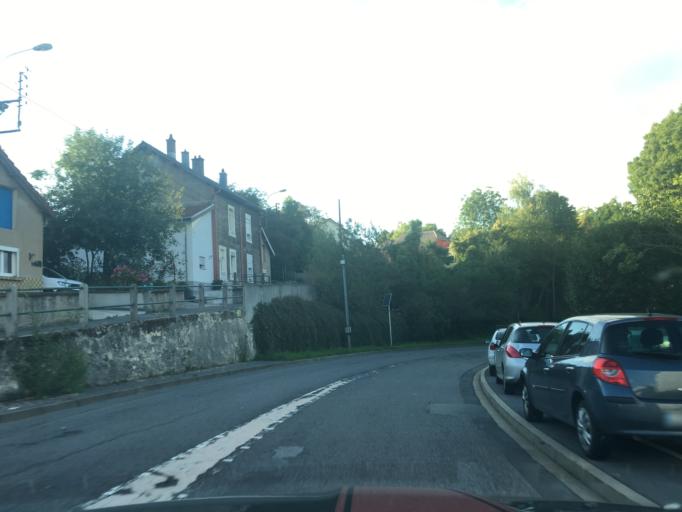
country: FR
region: Lorraine
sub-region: Departement de Meurthe-et-Moselle
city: Hussigny-Godbrange
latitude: 49.4991
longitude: 5.8635
